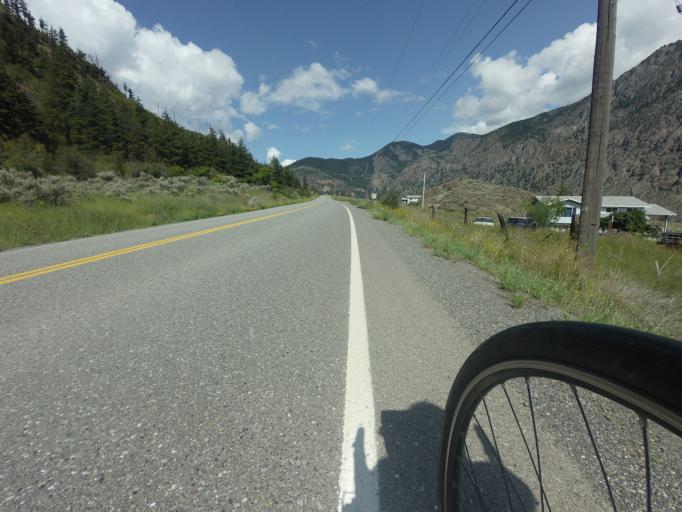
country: CA
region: British Columbia
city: Lillooet
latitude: 50.7564
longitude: -121.8973
